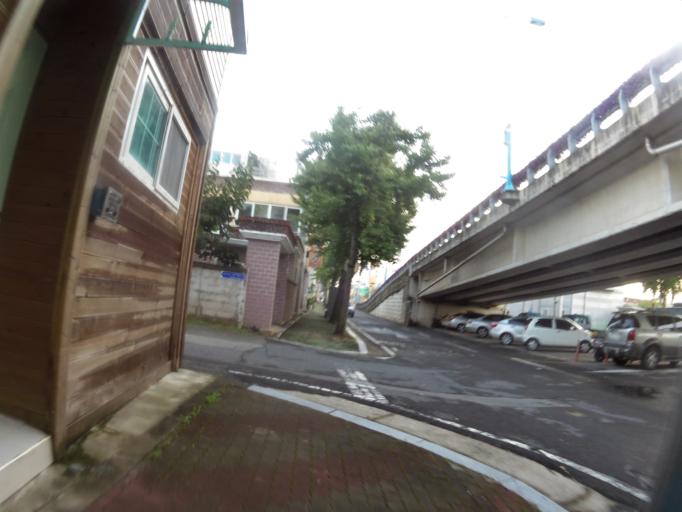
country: KR
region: Gyeongsangnam-do
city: Naeso
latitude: 35.3861
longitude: 128.4735
